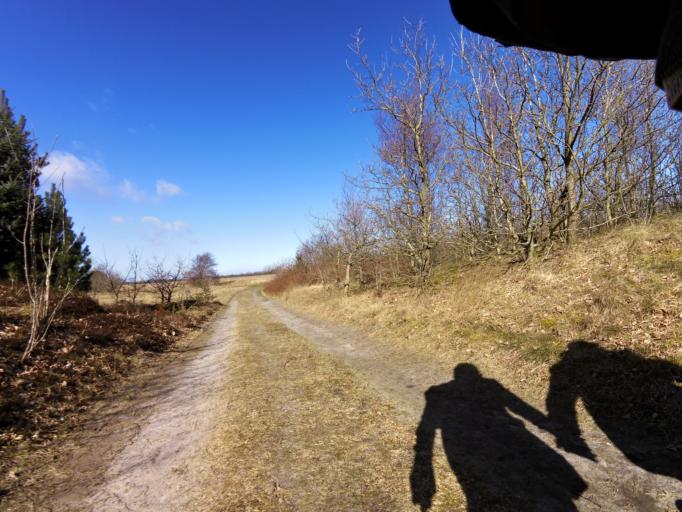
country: DK
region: South Denmark
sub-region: Varde Kommune
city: Varde
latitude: 55.5838
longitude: 8.3968
